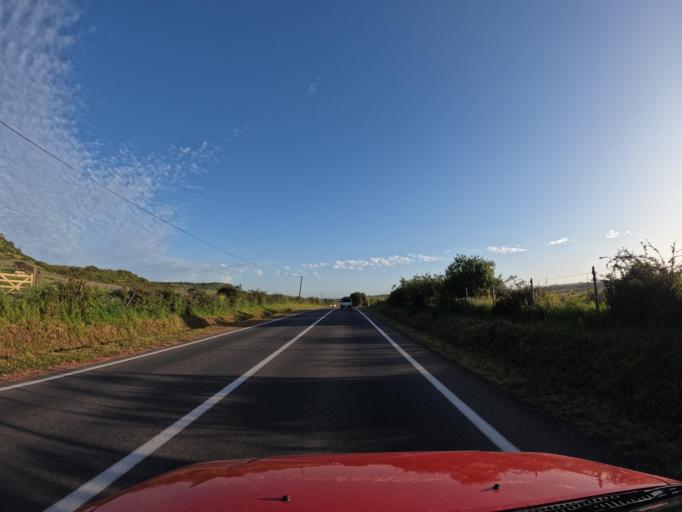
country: CL
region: O'Higgins
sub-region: Provincia de Colchagua
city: Santa Cruz
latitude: -34.1942
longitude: -71.7348
